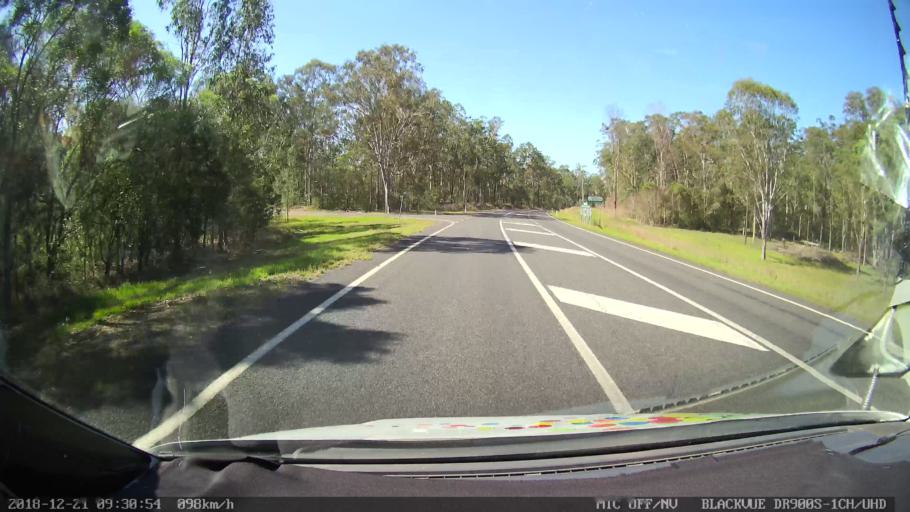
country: AU
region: New South Wales
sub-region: Clarence Valley
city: Maclean
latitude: -29.4534
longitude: 152.9937
